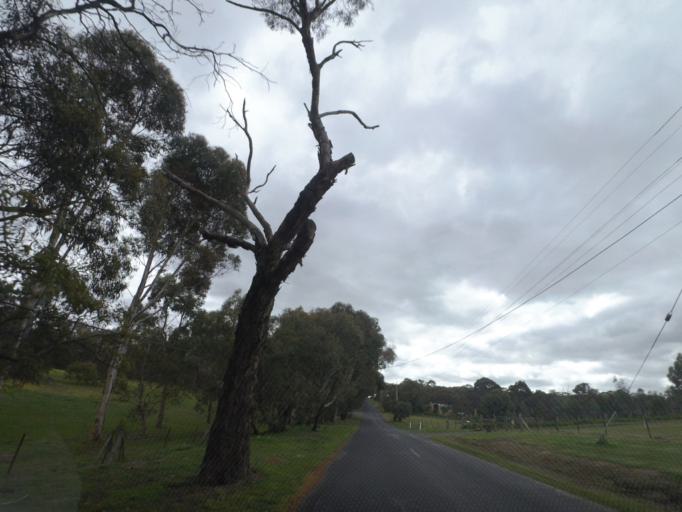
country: AU
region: Victoria
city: Plenty
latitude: -37.6685
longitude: 145.1100
